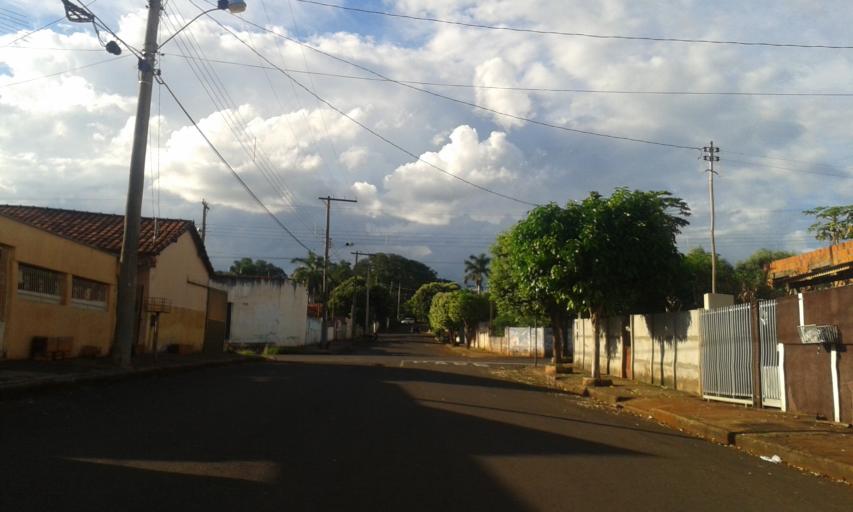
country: BR
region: Minas Gerais
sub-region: Ituiutaba
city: Ituiutaba
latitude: -18.9629
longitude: -49.4600
